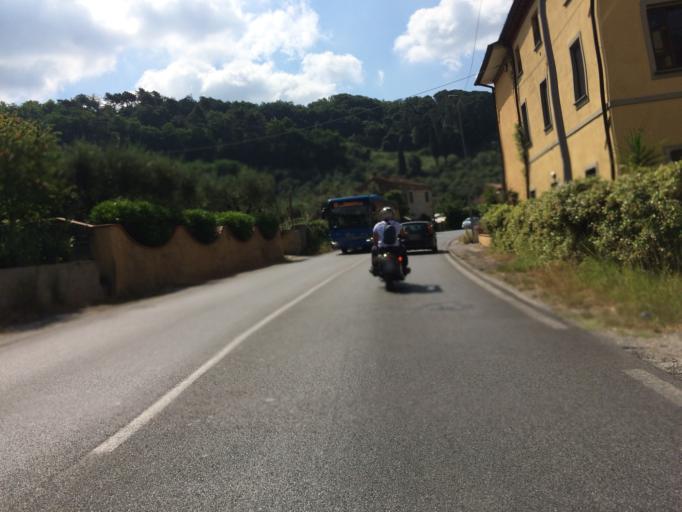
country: IT
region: Tuscany
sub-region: Provincia di Lucca
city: Massarosa
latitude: 43.8655
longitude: 10.3478
